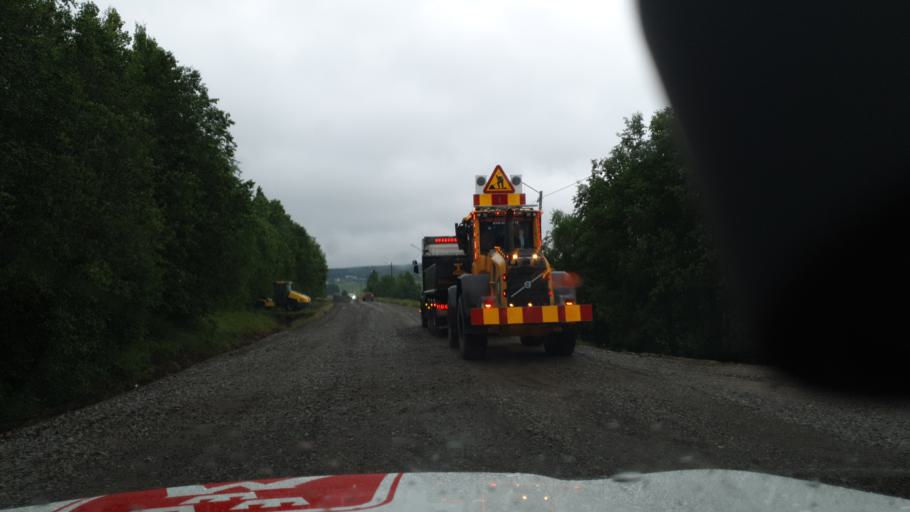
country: SE
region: Vaesterbotten
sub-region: Vannas Kommun
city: Vaennaes
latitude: 63.7368
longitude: 19.6533
